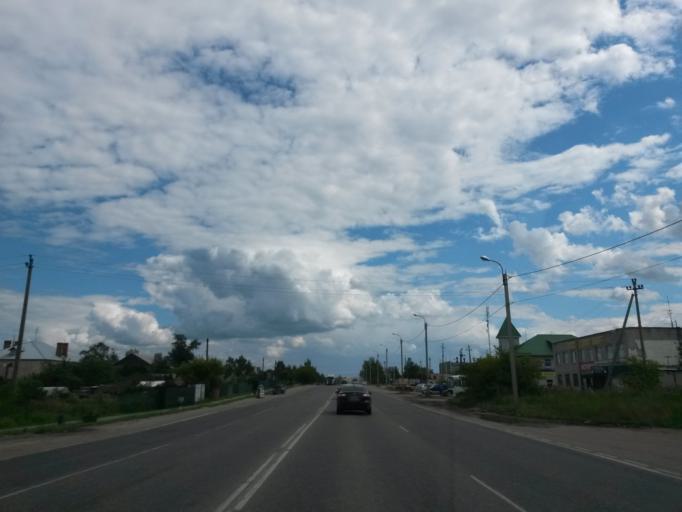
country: RU
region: Ivanovo
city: Novo-Talitsy
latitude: 57.0075
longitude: 40.8659
